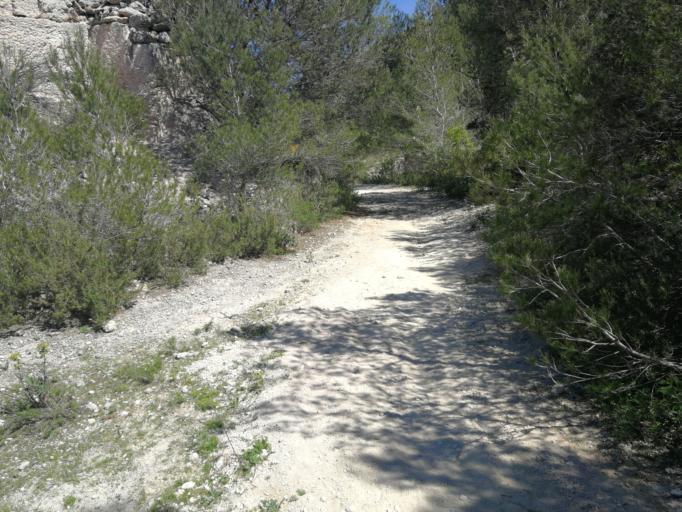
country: FR
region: Provence-Alpes-Cote d'Azur
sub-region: Departement des Bouches-du-Rhone
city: Sausset-les-Pins
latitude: 43.3440
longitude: 5.0500
